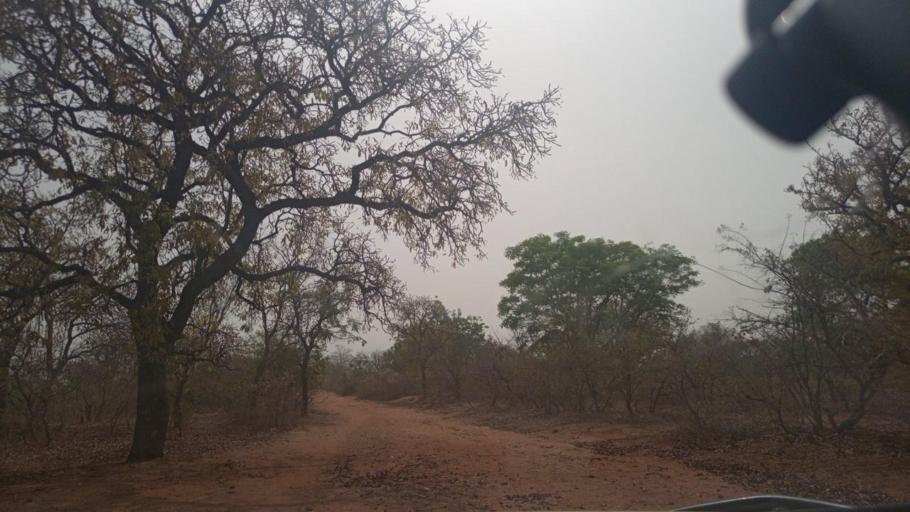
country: BF
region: Boucle du Mouhoun
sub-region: Province des Banwa
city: Salanso
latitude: 12.1887
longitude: -4.2154
